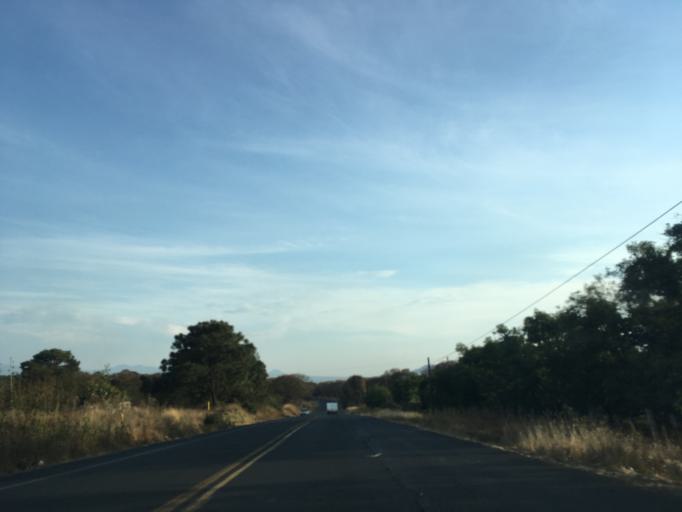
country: MX
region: Michoacan
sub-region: Tingueindin
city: Tingueindin
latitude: 19.6891
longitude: -102.4972
